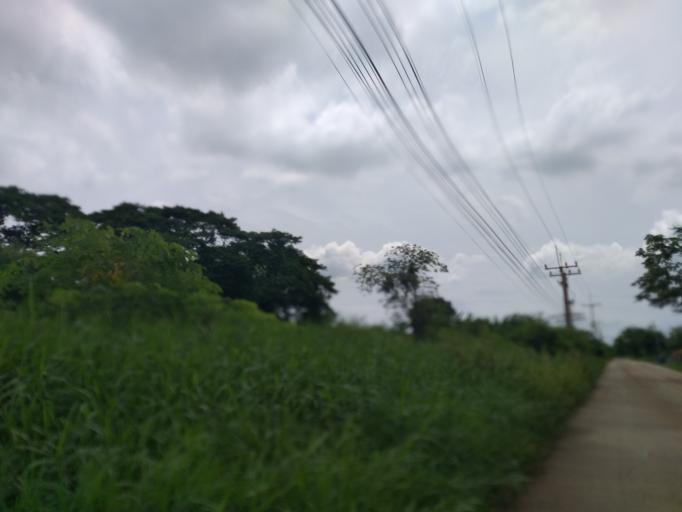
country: TH
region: Pathum Thani
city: Ban Lam Luk Ka
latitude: 13.9654
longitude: 100.8540
